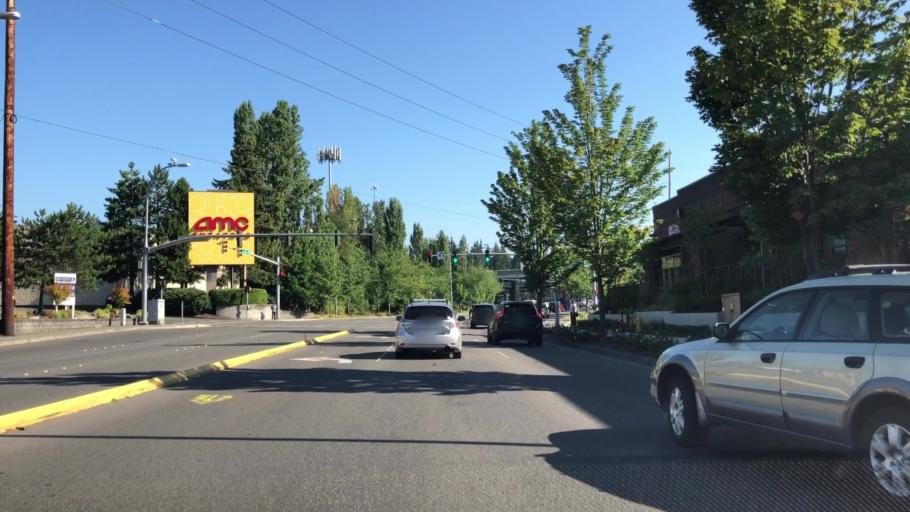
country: US
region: Washington
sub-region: King County
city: Newport
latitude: 47.5777
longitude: -122.1694
